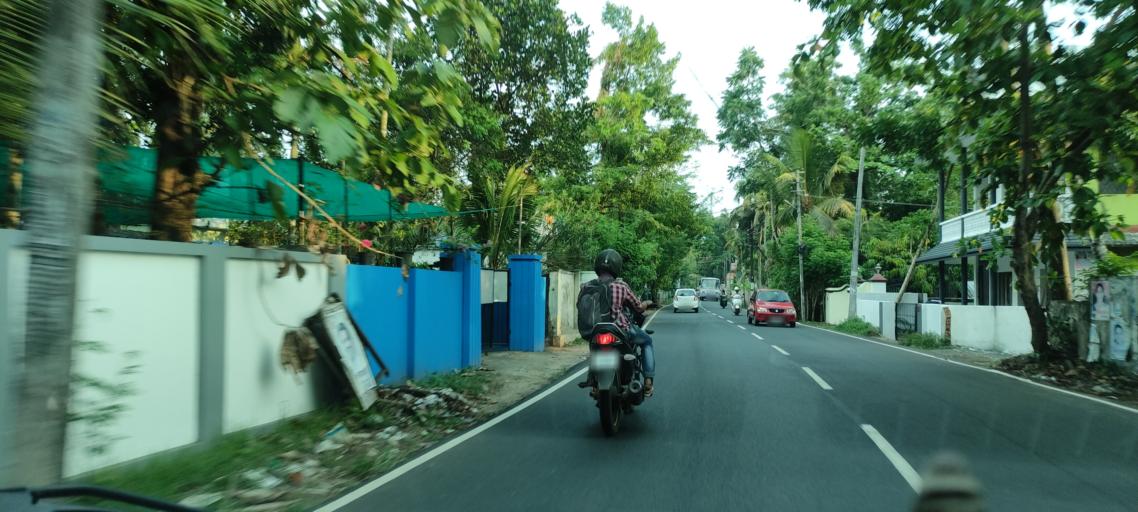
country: IN
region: Kerala
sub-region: Alappuzha
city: Arukutti
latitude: 9.8661
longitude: 76.3238
